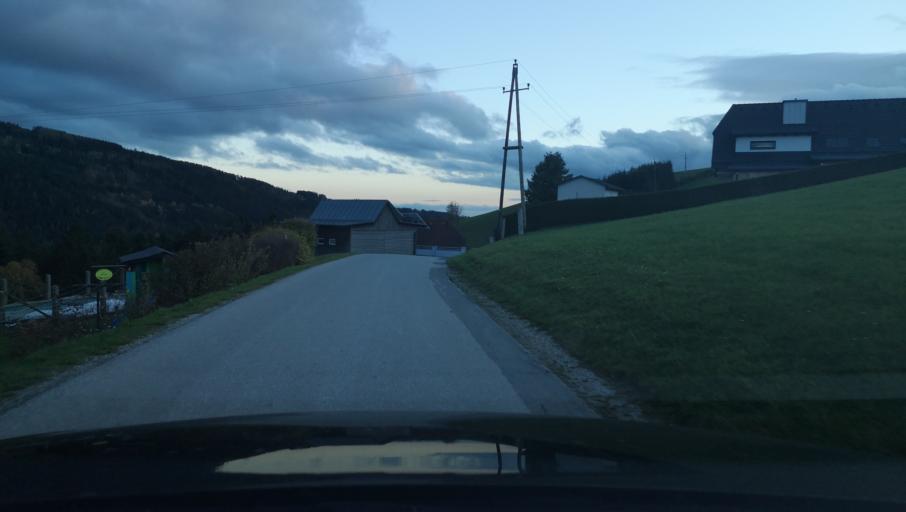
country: AT
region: Styria
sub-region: Politischer Bezirk Weiz
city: Koglhof
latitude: 47.3259
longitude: 15.6866
